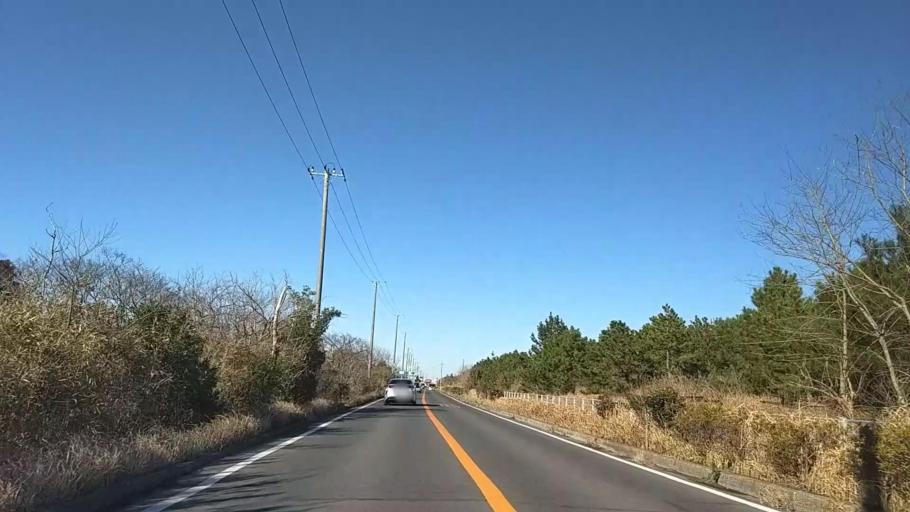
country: JP
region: Chiba
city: Ohara
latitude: 35.3361
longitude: 140.3916
